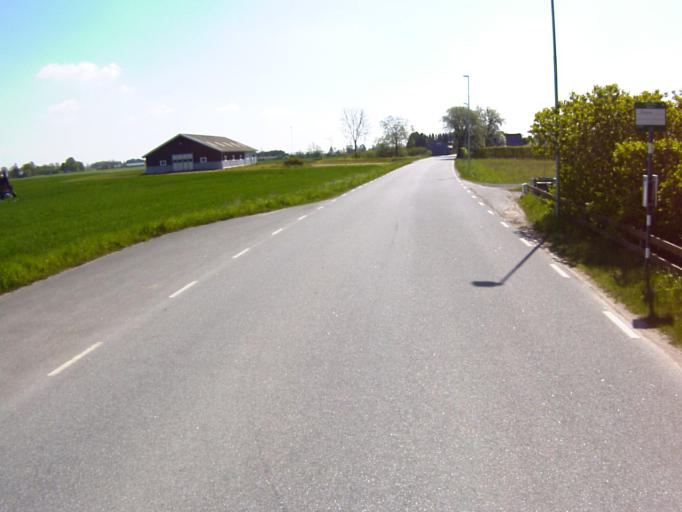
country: SE
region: Skane
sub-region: Kristianstads Kommun
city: Kristianstad
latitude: 56.0201
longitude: 14.2195
